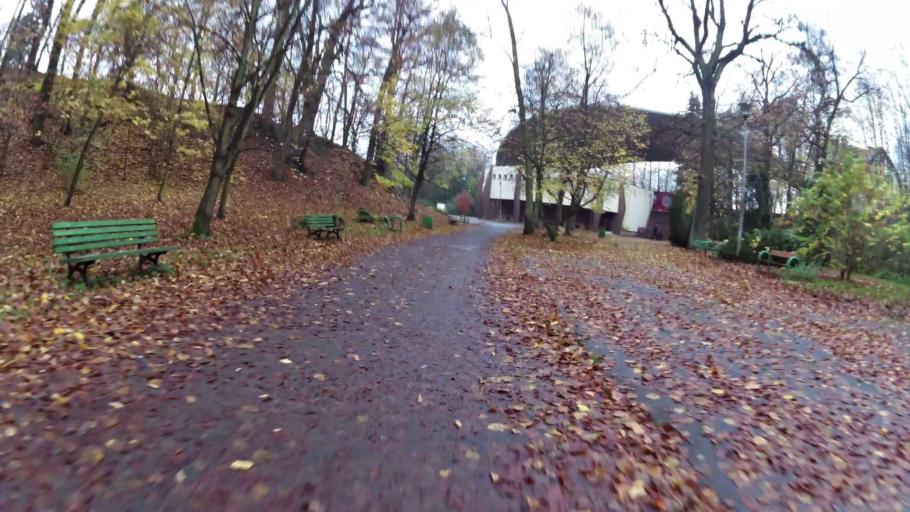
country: PL
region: West Pomeranian Voivodeship
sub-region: Koszalin
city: Koszalin
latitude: 54.1932
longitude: 16.1895
